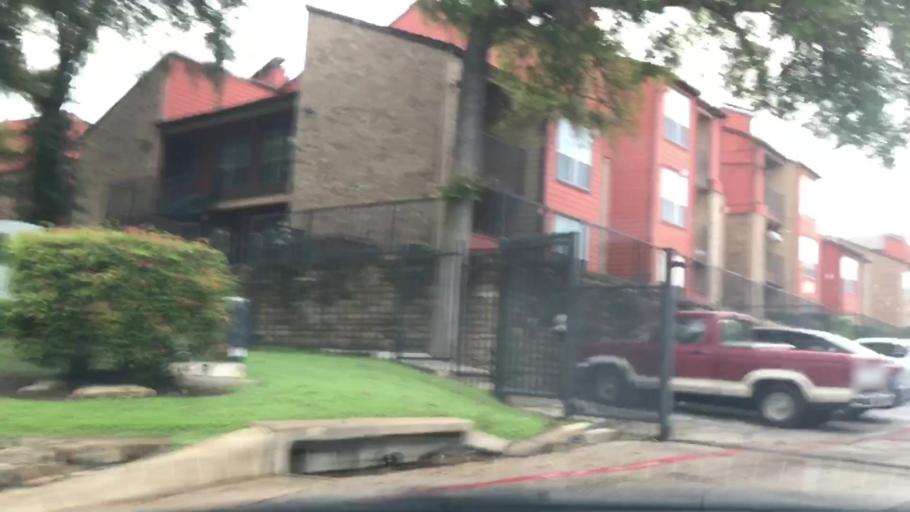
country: US
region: Texas
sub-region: Dallas County
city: Richardson
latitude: 32.8973
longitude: -96.7278
